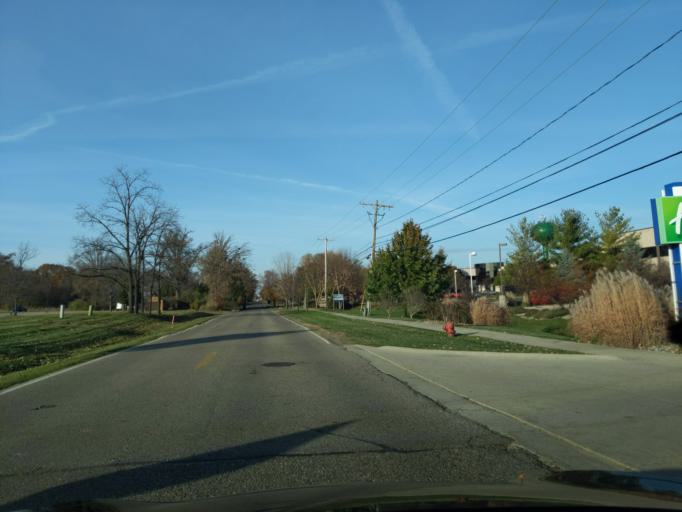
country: US
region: Michigan
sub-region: Ingham County
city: East Lansing
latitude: 42.7631
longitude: -84.5084
